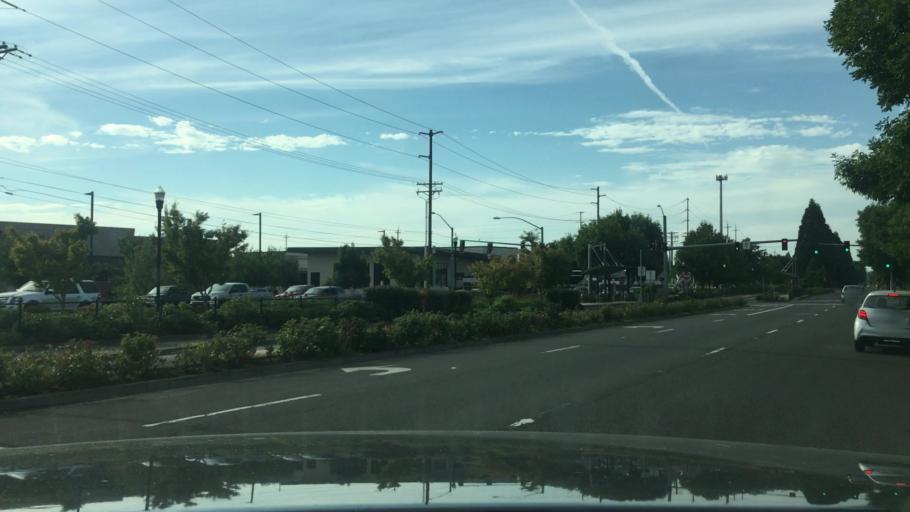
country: US
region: Oregon
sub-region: Lane County
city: Springfield
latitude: 44.0622
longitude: -123.0258
